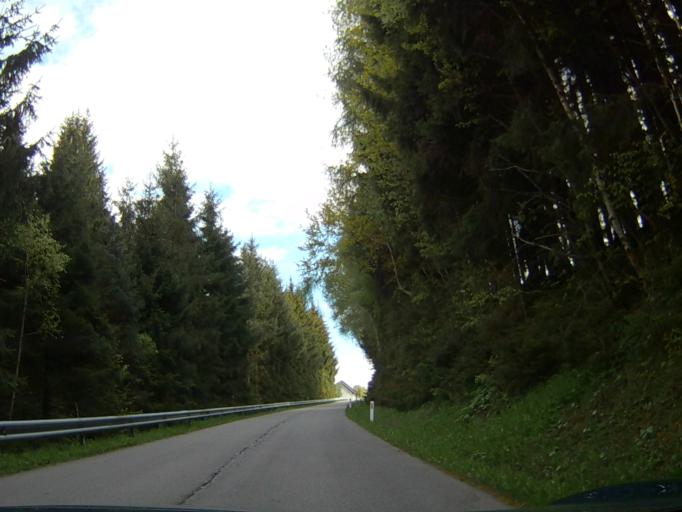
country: AT
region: Carinthia
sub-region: Politischer Bezirk Villach Land
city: Stockenboi
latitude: 46.7352
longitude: 13.5652
